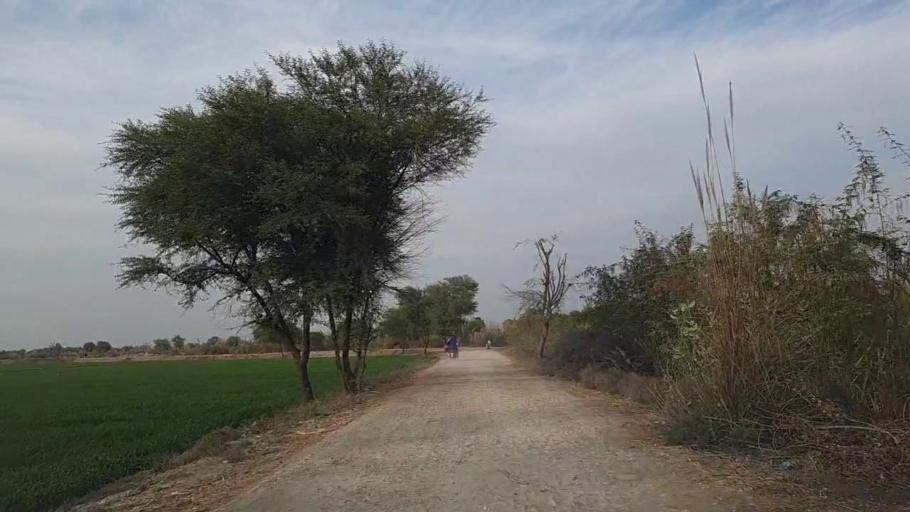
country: PK
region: Sindh
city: Daur
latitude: 26.5247
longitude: 68.4073
